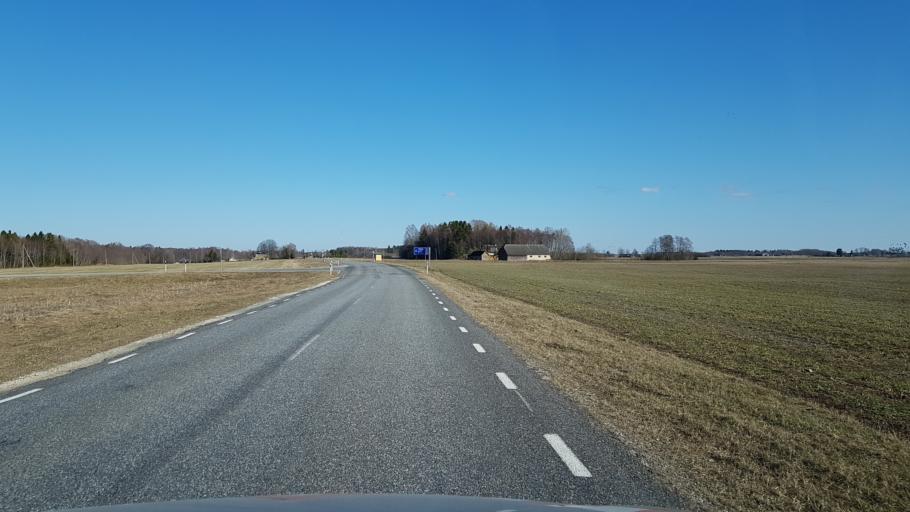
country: EE
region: Laeaene-Virumaa
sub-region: Haljala vald
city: Haljala
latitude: 59.4631
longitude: 26.1942
